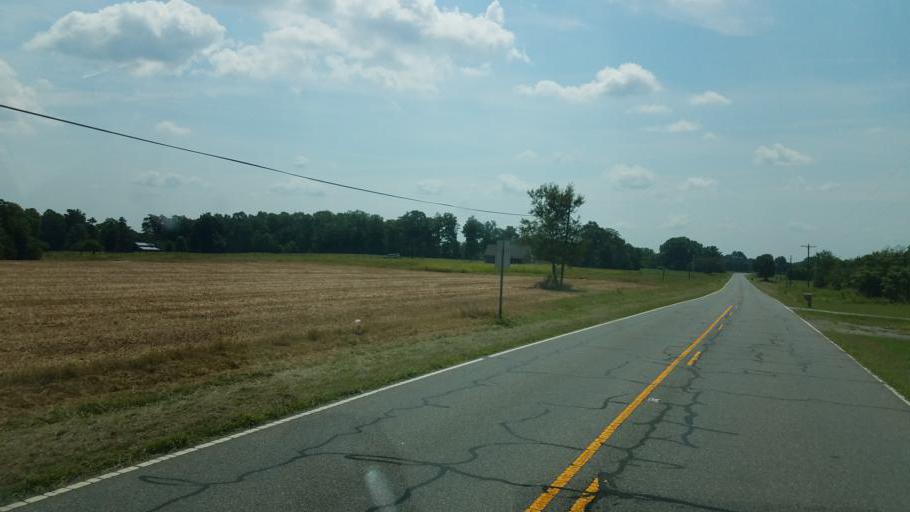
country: US
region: North Carolina
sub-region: Gaston County
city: Cherryville
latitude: 35.4348
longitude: -81.4186
